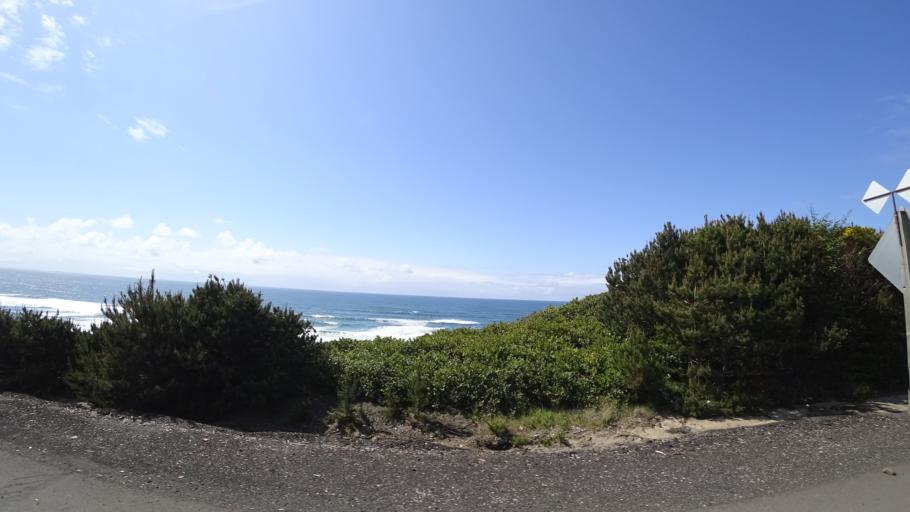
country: US
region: Oregon
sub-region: Lincoln County
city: Newport
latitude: 44.7094
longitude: -124.0598
